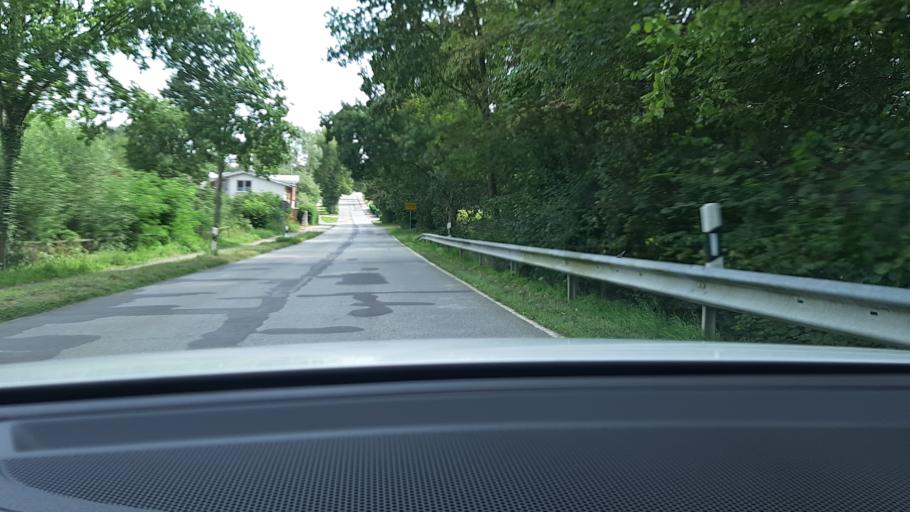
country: DE
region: Schleswig-Holstein
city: Heilshoop
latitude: 53.8916
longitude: 10.5269
